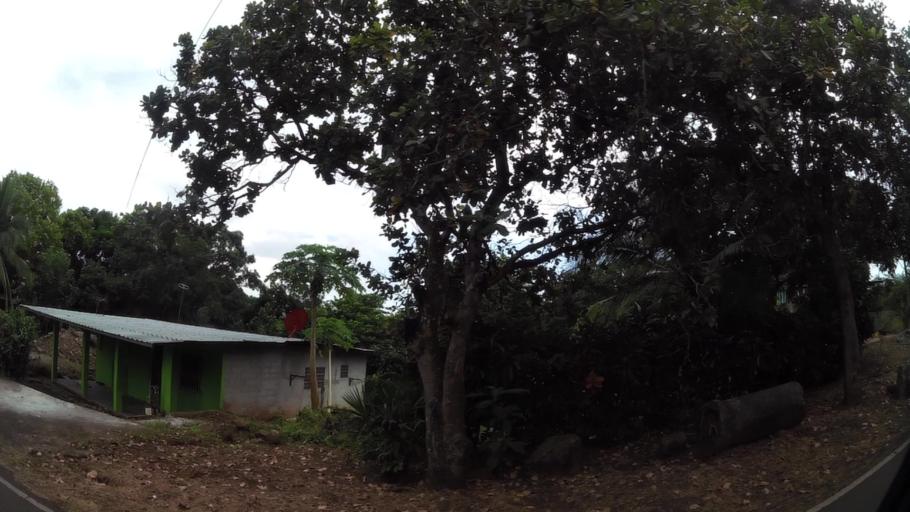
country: PA
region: Panama
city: Tocumen
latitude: 9.1170
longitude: -79.3750
